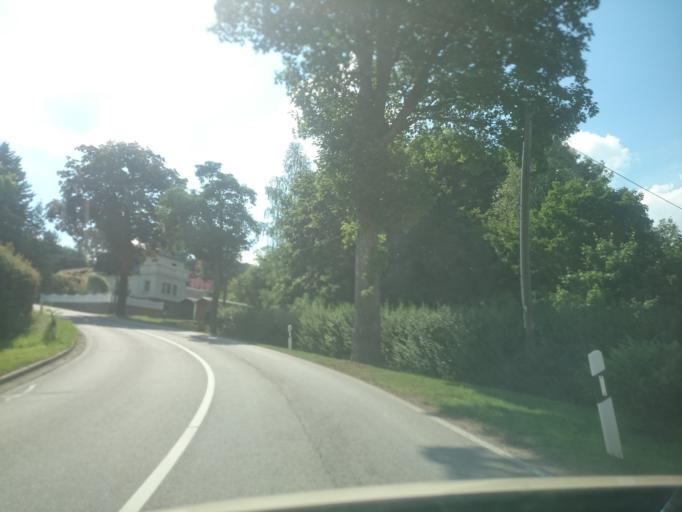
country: DE
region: Saxony
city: Pockau
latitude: 50.7106
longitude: 13.2187
